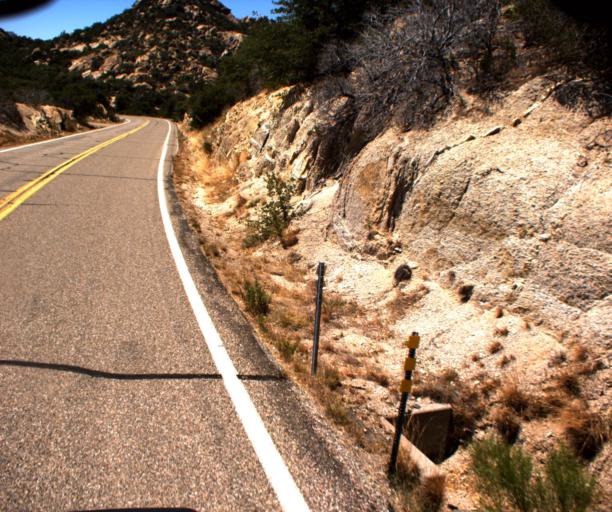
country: US
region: Arizona
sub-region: Pima County
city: Sells
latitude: 31.9504
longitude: -111.6200
